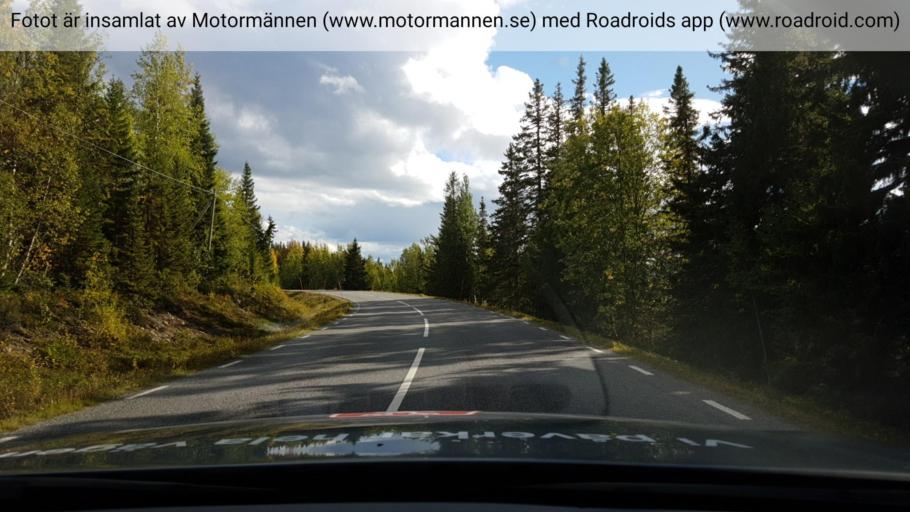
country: SE
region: Jaemtland
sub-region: Are Kommun
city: Are
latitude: 63.4880
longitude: 13.1858
